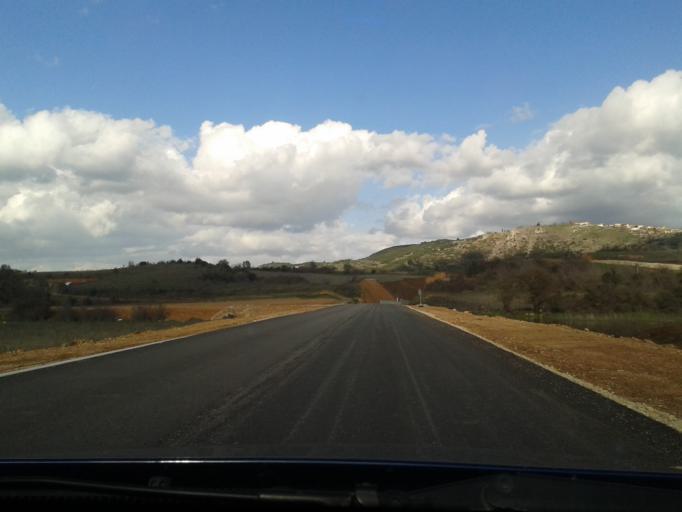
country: GR
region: West Greece
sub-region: Nomos Aitolias kai Akarnanias
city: Fitiai
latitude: 38.6842
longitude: 21.1685
